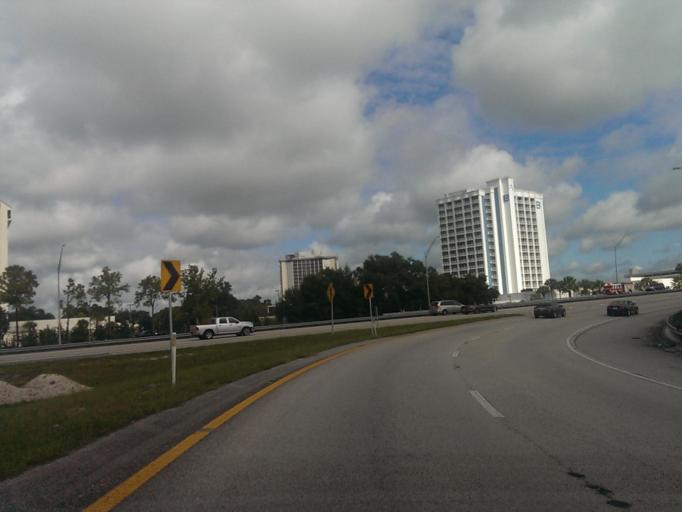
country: US
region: Florida
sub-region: Osceola County
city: Celebration
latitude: 28.3740
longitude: -81.5065
